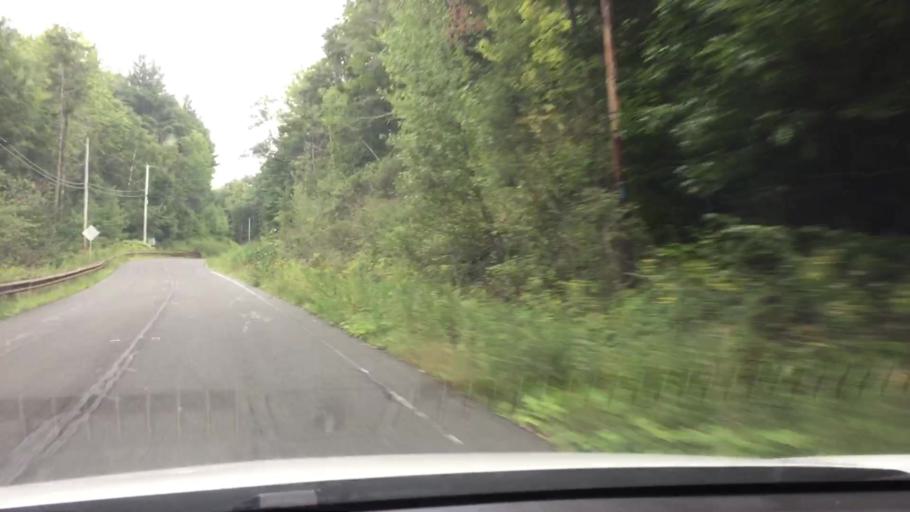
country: US
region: Massachusetts
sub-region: Berkshire County
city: Becket
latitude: 42.2642
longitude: -73.0016
